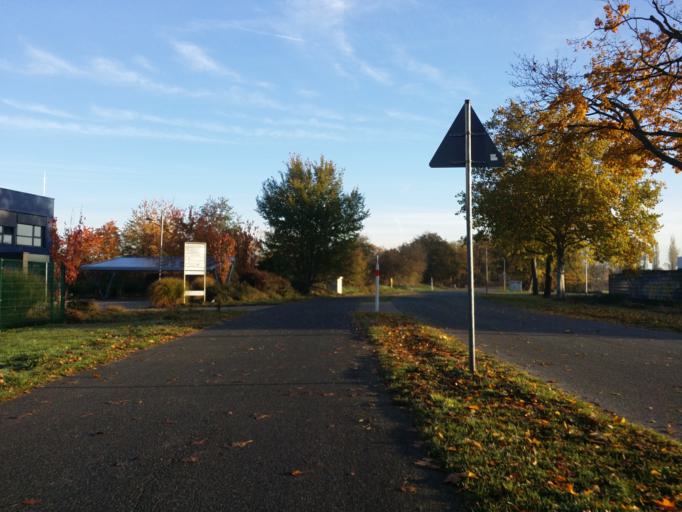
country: DE
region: Lower Saxony
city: Stuhr
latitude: 53.0208
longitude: 8.7913
